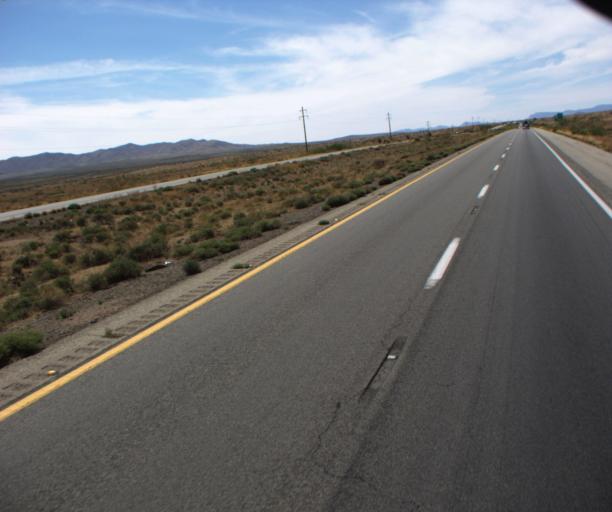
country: US
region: Arizona
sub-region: Cochise County
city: Willcox
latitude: 32.3620
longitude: -109.6542
